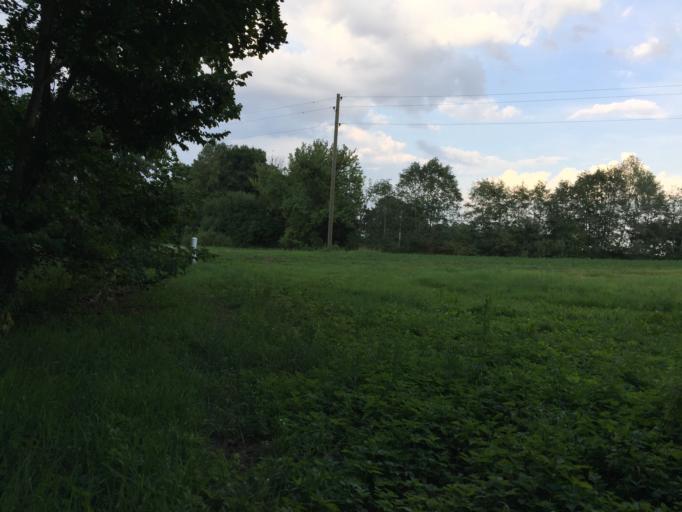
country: LV
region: Dobeles Rajons
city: Dobele
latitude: 56.5999
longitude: 23.3061
